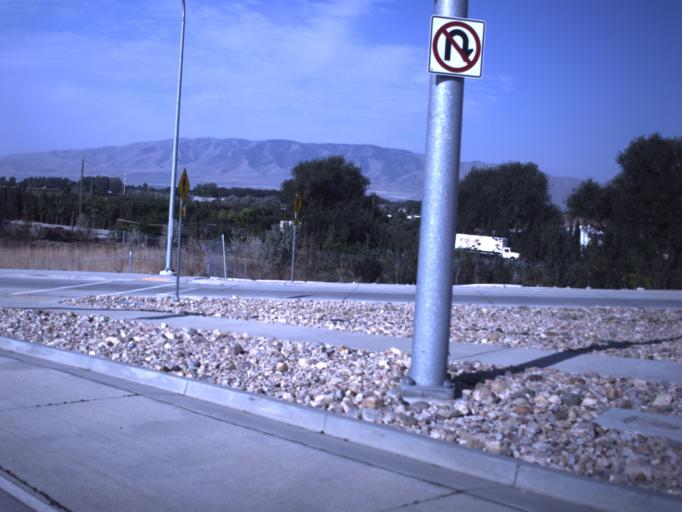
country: US
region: Utah
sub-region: Utah County
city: American Fork
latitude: 40.3594
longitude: -111.7856
